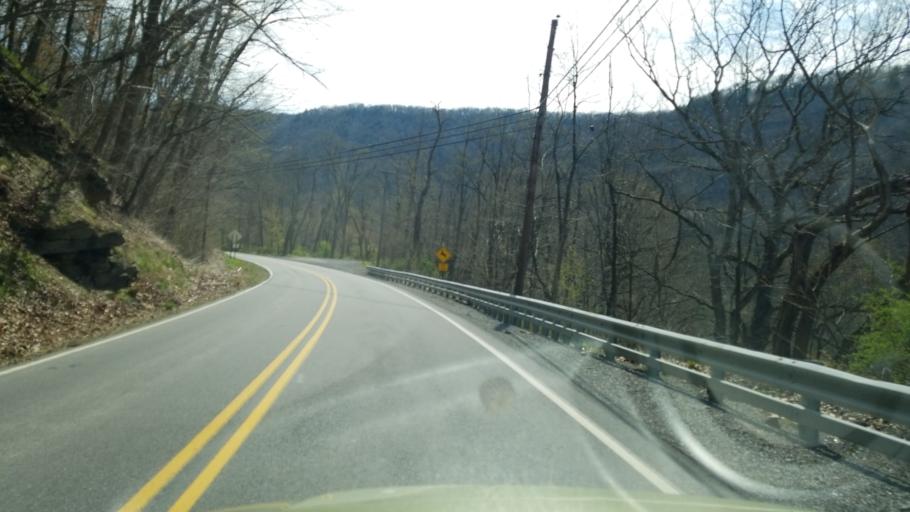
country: US
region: Pennsylvania
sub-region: Clinton County
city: Renovo
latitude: 41.3041
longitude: -77.8118
